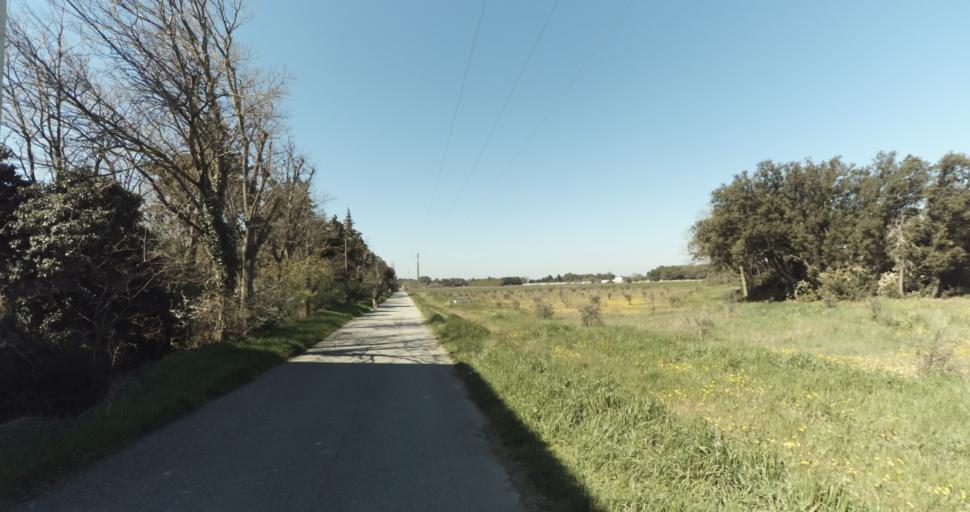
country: FR
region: Provence-Alpes-Cote d'Azur
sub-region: Departement des Bouches-du-Rhone
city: Pelissanne
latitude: 43.6116
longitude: 5.1532
